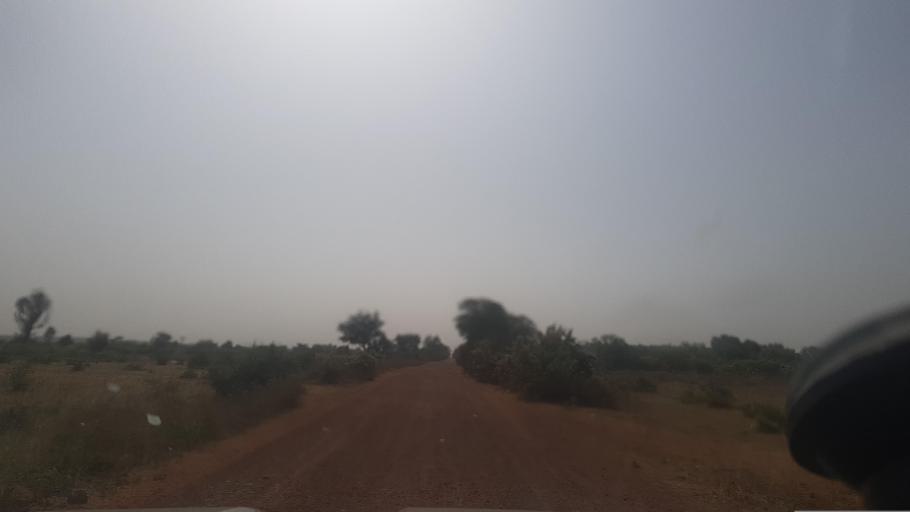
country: ML
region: Segou
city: Baroueli
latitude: 13.1417
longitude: -6.5141
